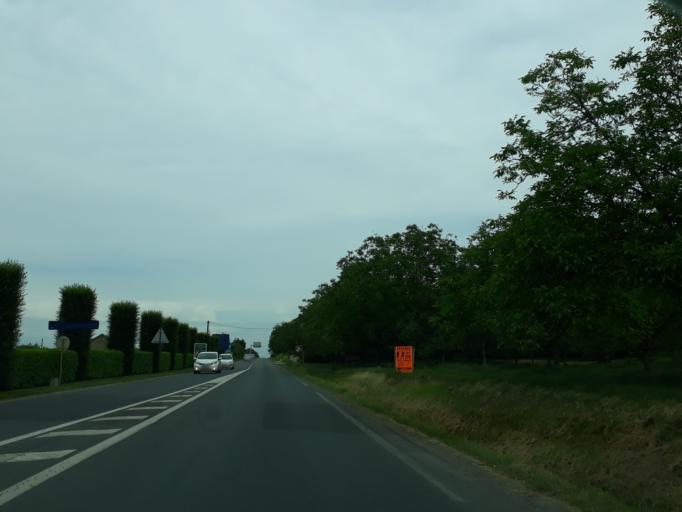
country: FR
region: Aquitaine
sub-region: Departement de la Dordogne
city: Terrasson-Lavilledieu
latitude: 45.1282
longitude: 1.3260
